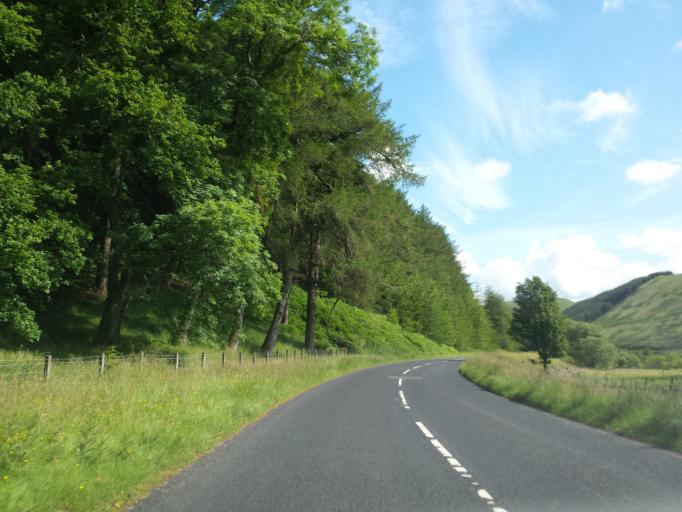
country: GB
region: Scotland
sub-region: The Scottish Borders
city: Peebles
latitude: 55.4599
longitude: -3.2166
